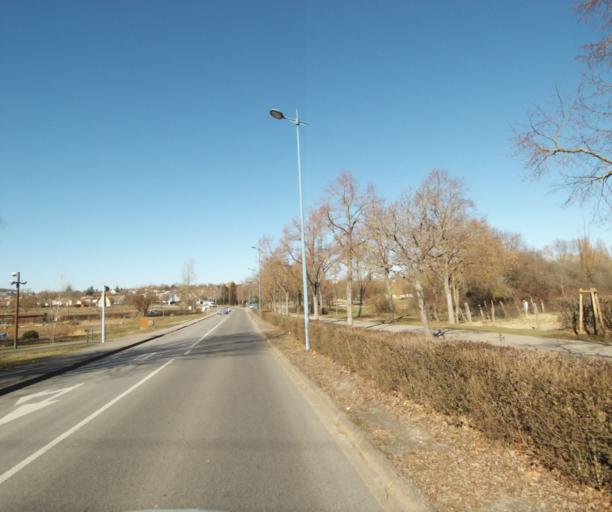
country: FR
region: Lorraine
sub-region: Departement de Meurthe-et-Moselle
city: Vandoeuvre-les-Nancy
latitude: 48.6467
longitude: 6.1973
